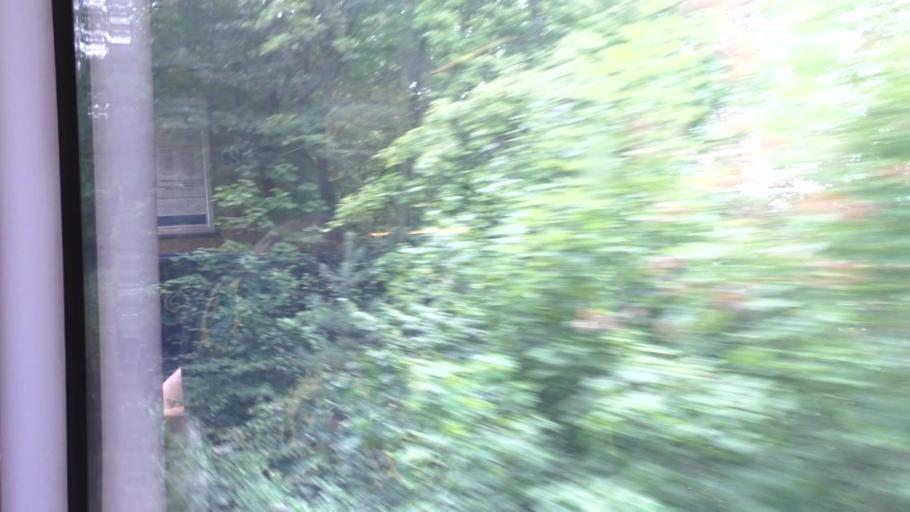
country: DE
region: Saxony
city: Hirschfelde
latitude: 50.9547
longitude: 14.8968
